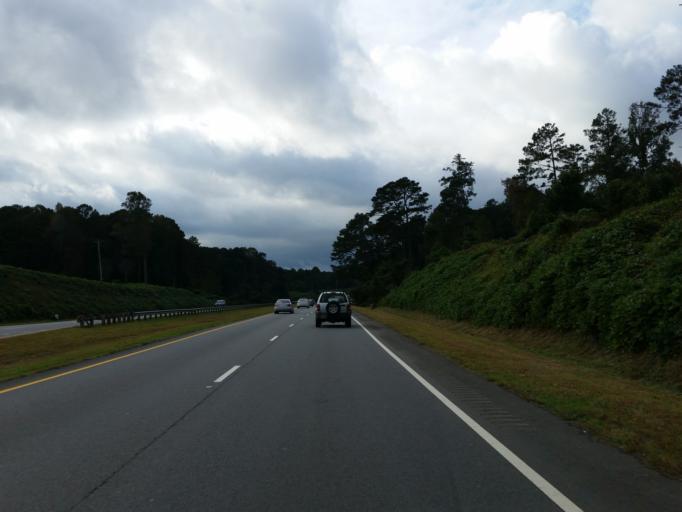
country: US
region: Georgia
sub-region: Cobb County
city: Acworth
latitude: 34.0574
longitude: -84.7144
